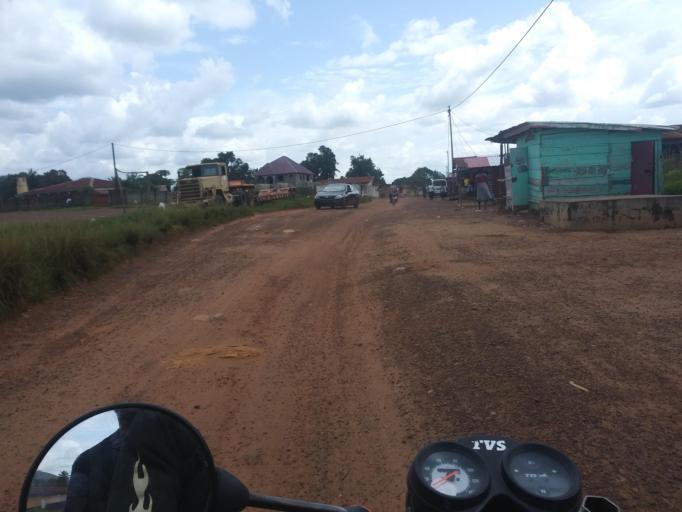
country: SL
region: Northern Province
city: Makeni
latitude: 8.8753
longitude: -12.0426
